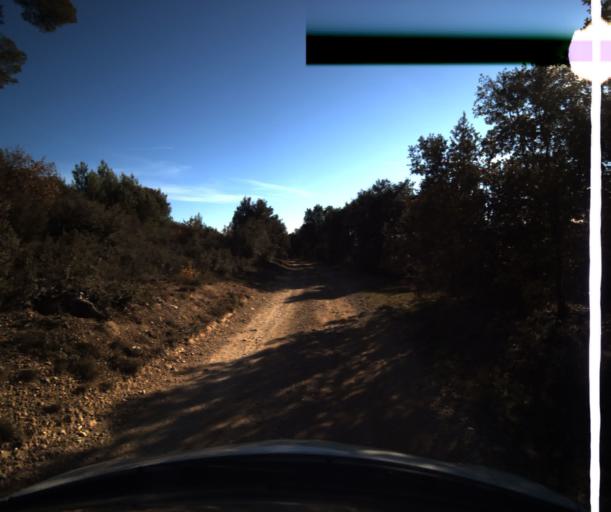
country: FR
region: Provence-Alpes-Cote d'Azur
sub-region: Departement du Vaucluse
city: Villelaure
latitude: 43.7040
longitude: 5.4601
